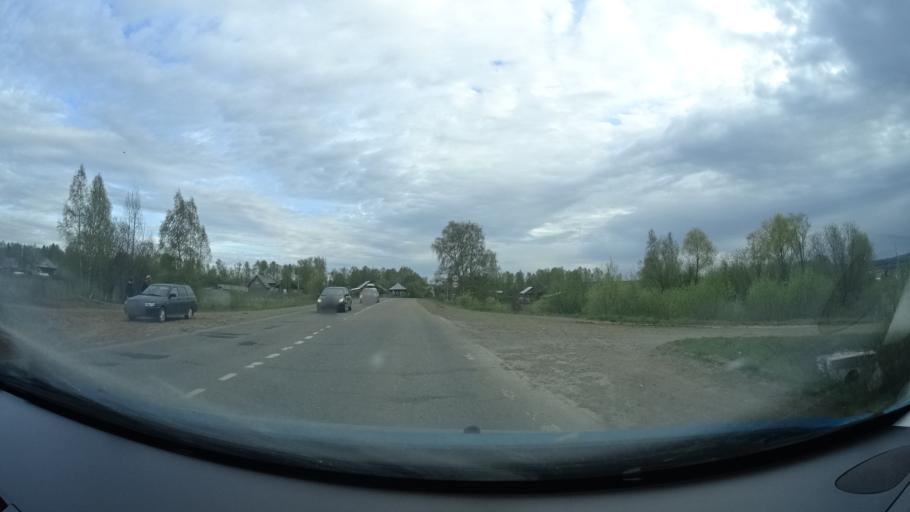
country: RU
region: Perm
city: Osa
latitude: 57.3757
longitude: 55.6096
